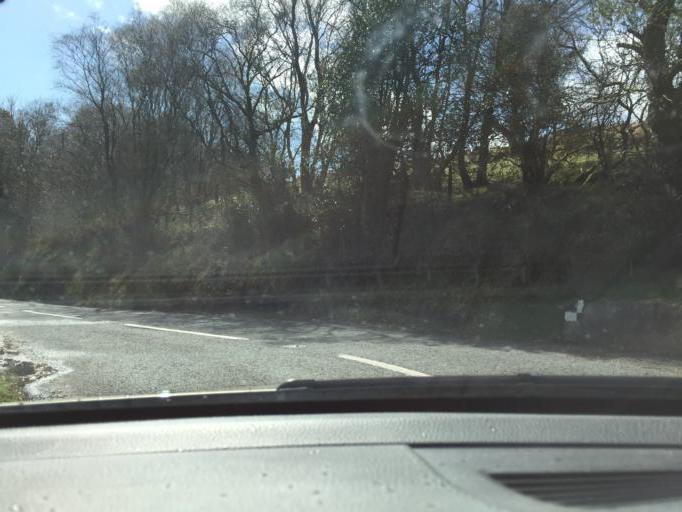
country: GB
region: Northern Ireland
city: Cushendall
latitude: 55.1284
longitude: -6.0864
